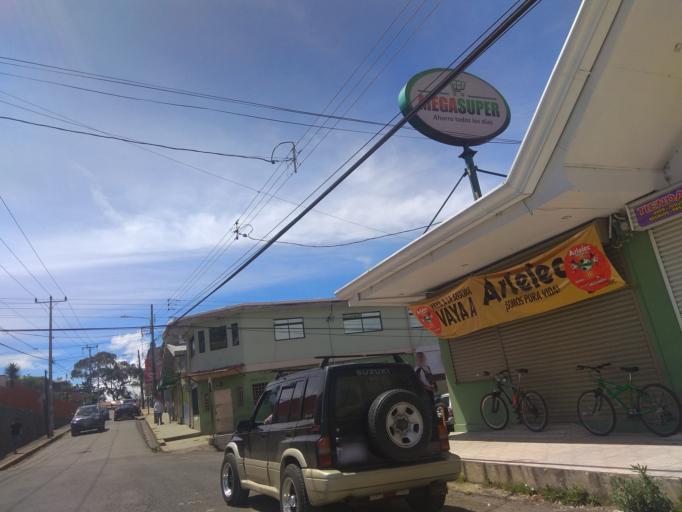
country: CR
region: Cartago
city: Cot
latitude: 9.9152
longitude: -83.8935
